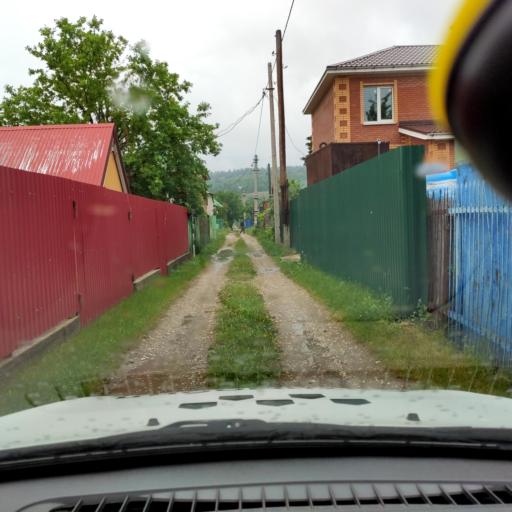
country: RU
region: Samara
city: Povolzhskiy
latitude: 53.4635
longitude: 49.6520
